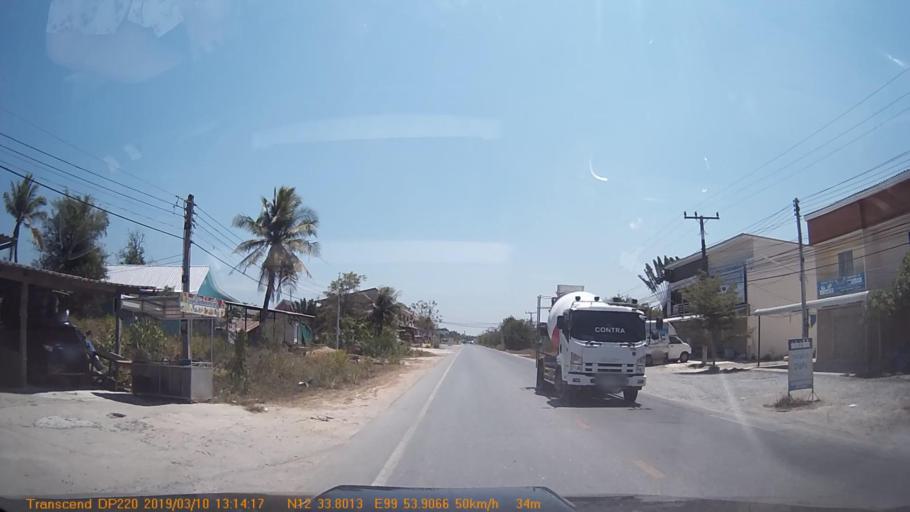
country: TH
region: Prachuap Khiri Khan
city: Hua Hin
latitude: 12.5631
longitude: 99.8985
